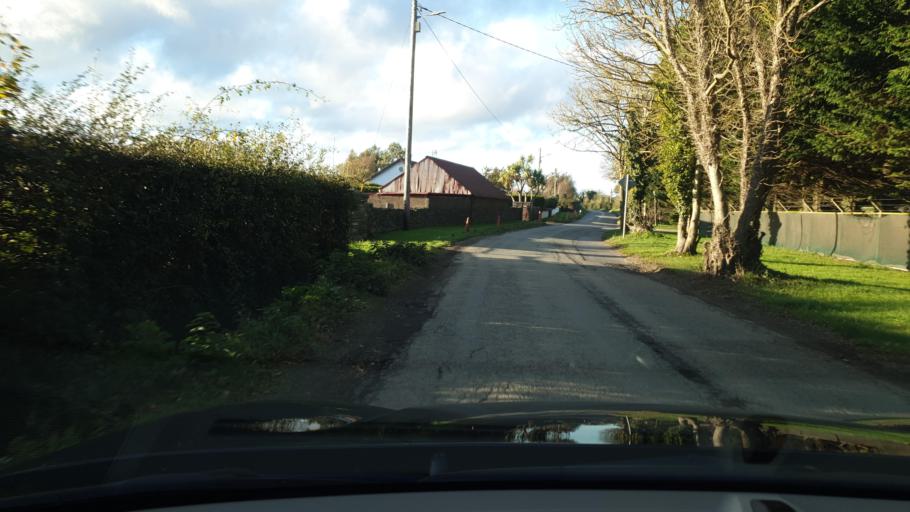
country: IE
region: Leinster
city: Balrothery
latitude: 53.5919
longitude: -6.2078
